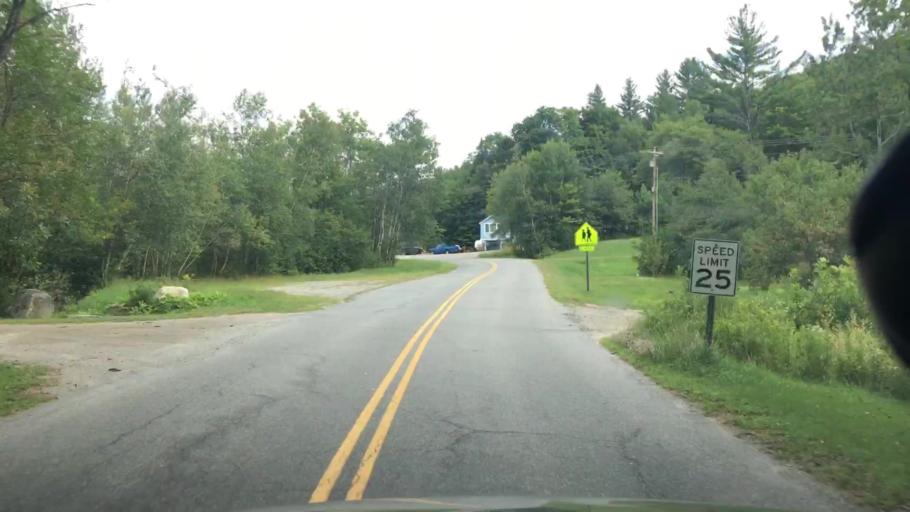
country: US
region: Massachusetts
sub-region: Franklin County
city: Colrain
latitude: 42.7832
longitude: -72.7684
